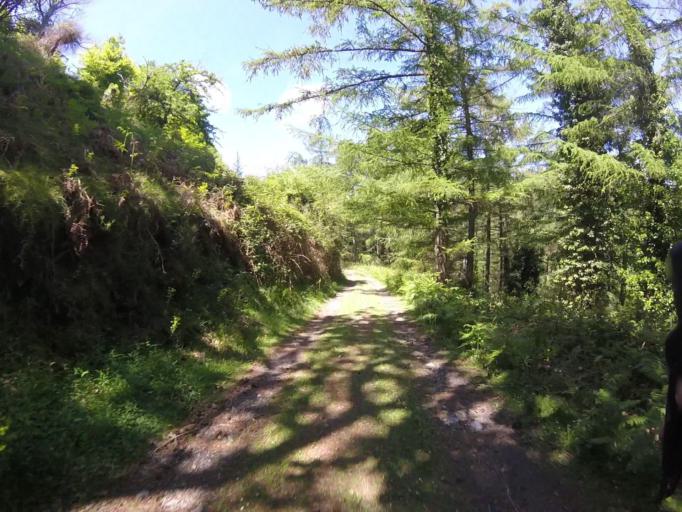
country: ES
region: Navarre
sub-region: Provincia de Navarra
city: Lesaka
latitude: 43.2502
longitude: -1.7585
